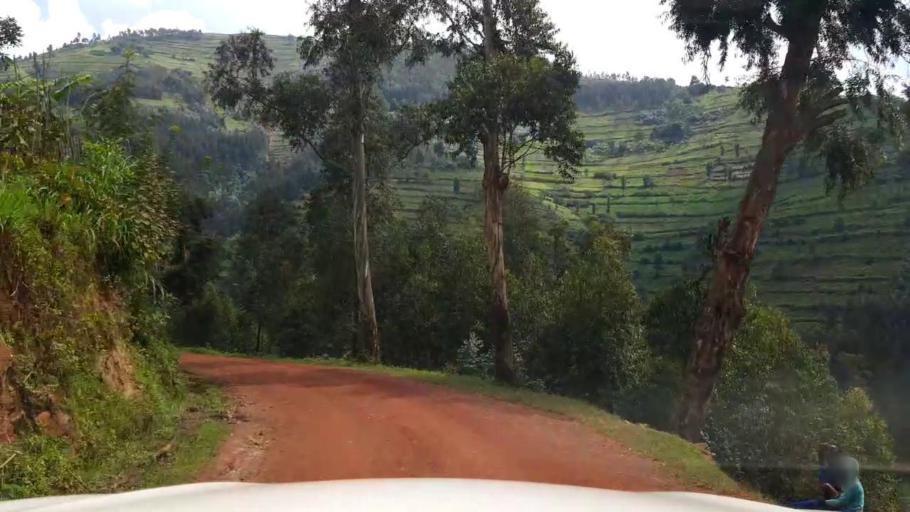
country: UG
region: Western Region
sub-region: Kisoro District
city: Kisoro
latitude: -1.3824
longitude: 29.7943
